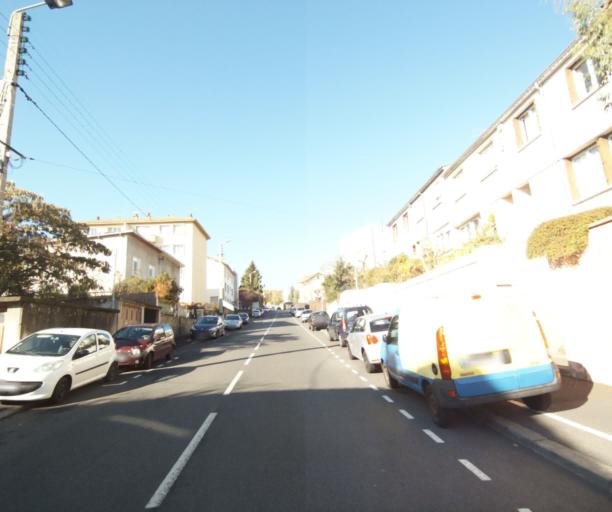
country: FR
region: Auvergne
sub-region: Departement du Puy-de-Dome
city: Chamalieres
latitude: 45.7877
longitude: 3.0673
